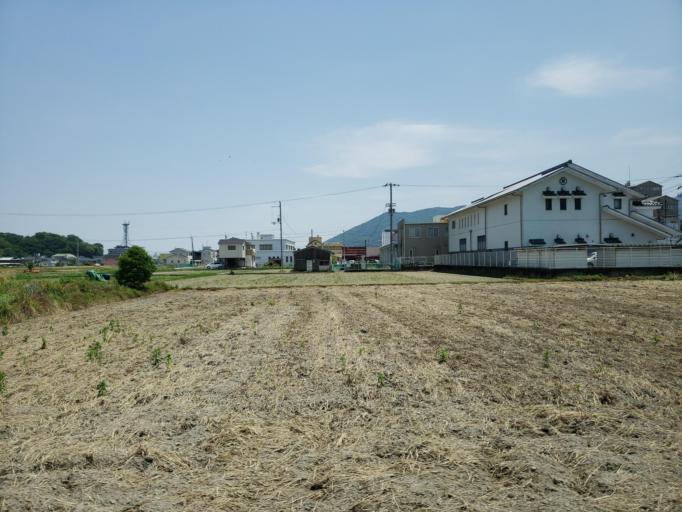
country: JP
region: Tokushima
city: Wakimachi
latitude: 34.0651
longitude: 134.1547
